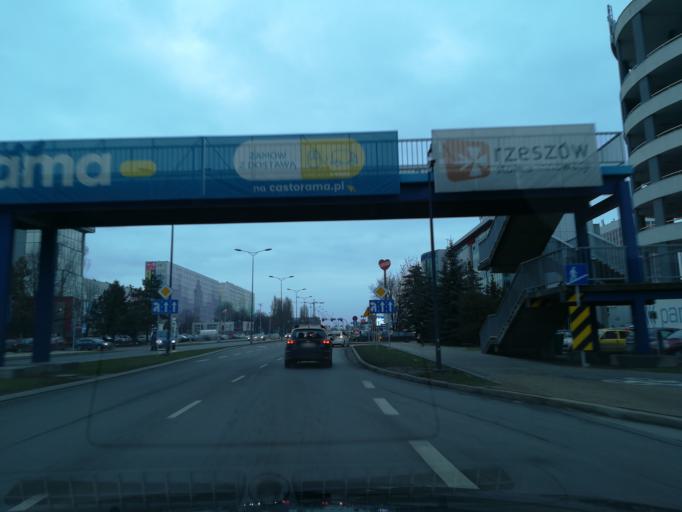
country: PL
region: Subcarpathian Voivodeship
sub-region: Rzeszow
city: Rzeszow
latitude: 50.0197
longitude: 22.0173
